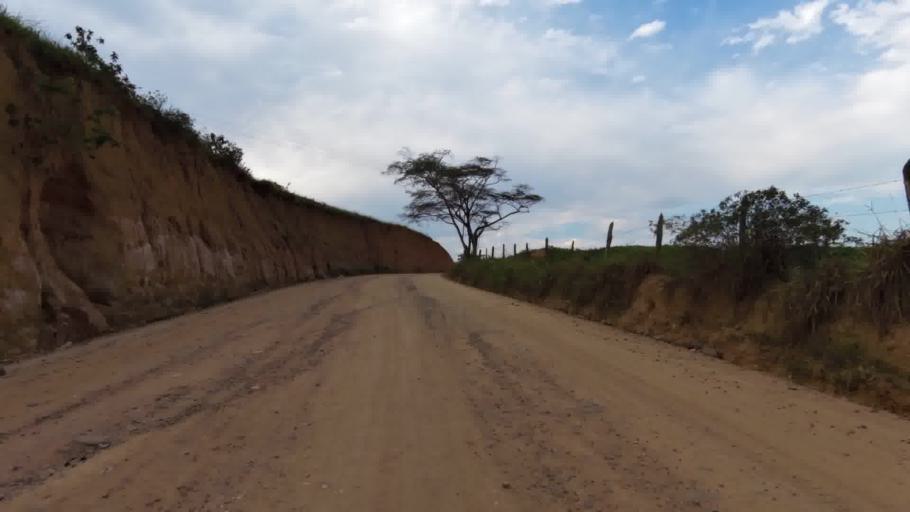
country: BR
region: Espirito Santo
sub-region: Piuma
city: Piuma
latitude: -20.8357
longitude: -40.7436
